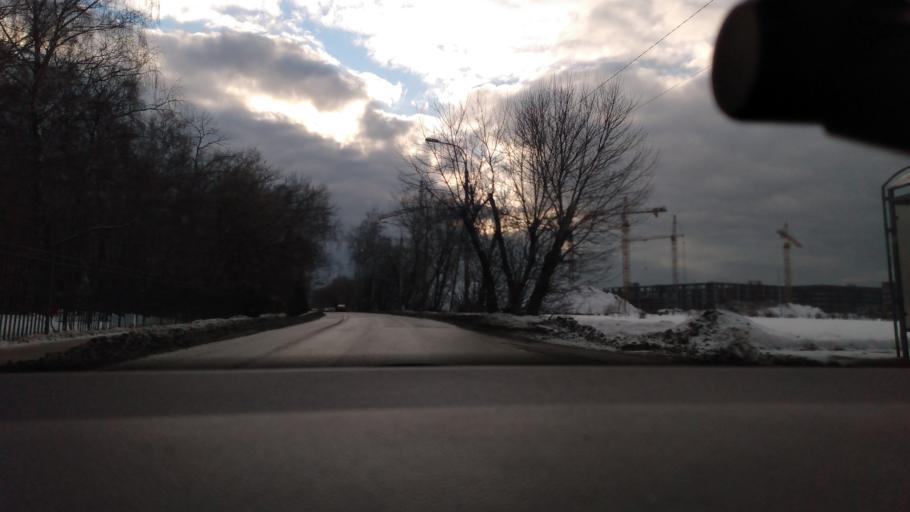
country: RU
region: Moskovskaya
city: Zheleznodorozhnyy
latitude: 55.7340
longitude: 38.0370
